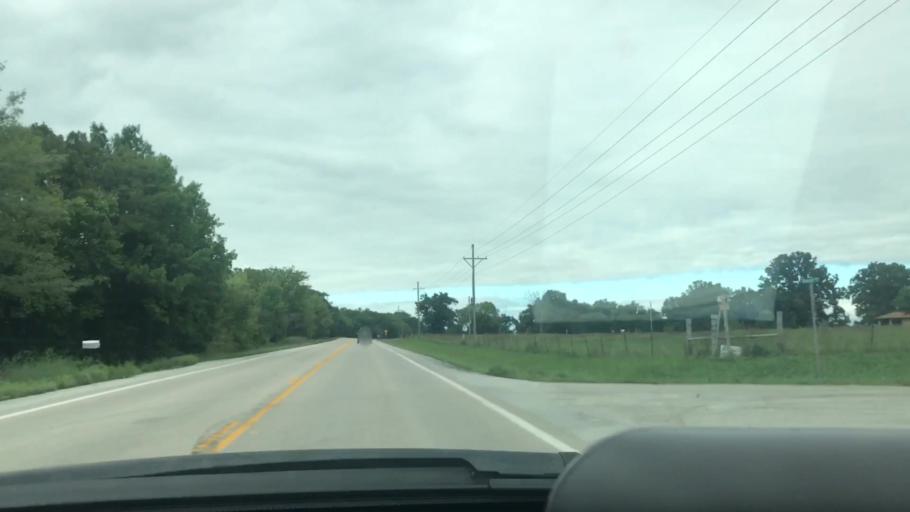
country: US
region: Missouri
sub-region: Hickory County
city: Hermitage
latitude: 37.8680
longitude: -93.1797
